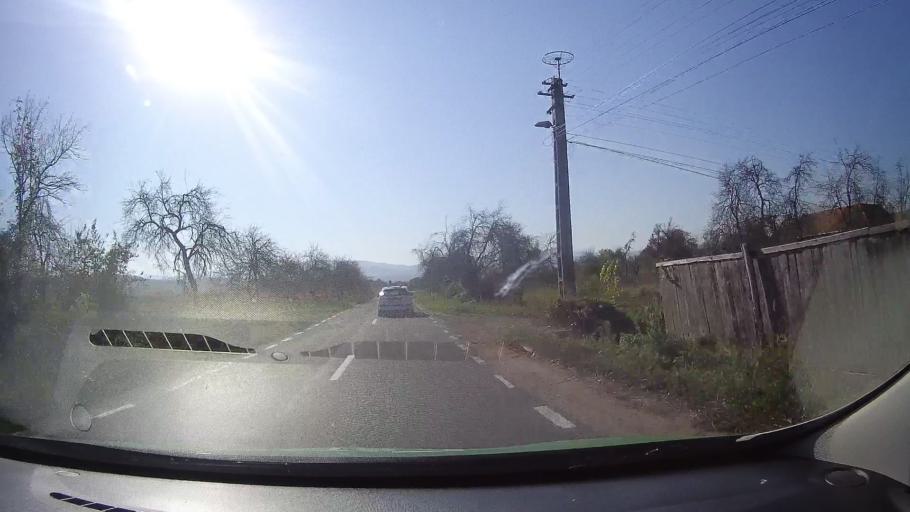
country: RO
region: Timis
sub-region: Comuna Curtea
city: Curtea
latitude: 45.8477
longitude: 22.3134
